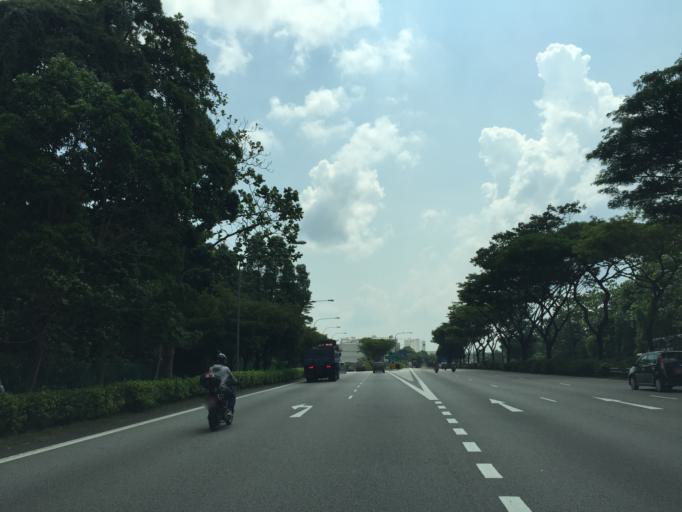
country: MY
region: Johor
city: Johor Bahru
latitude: 1.4281
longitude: 103.7699
